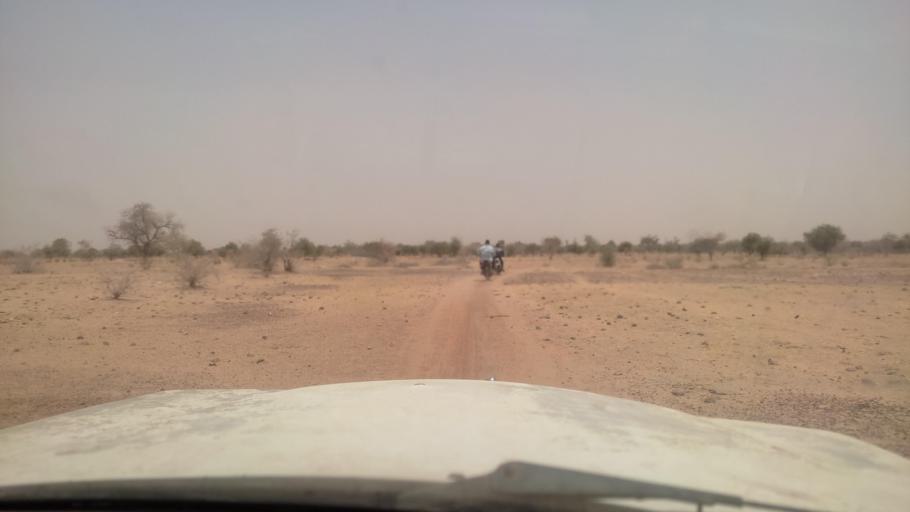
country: BF
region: Est
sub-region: Gnagna Province
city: Bogande
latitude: 13.0021
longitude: -0.0952
